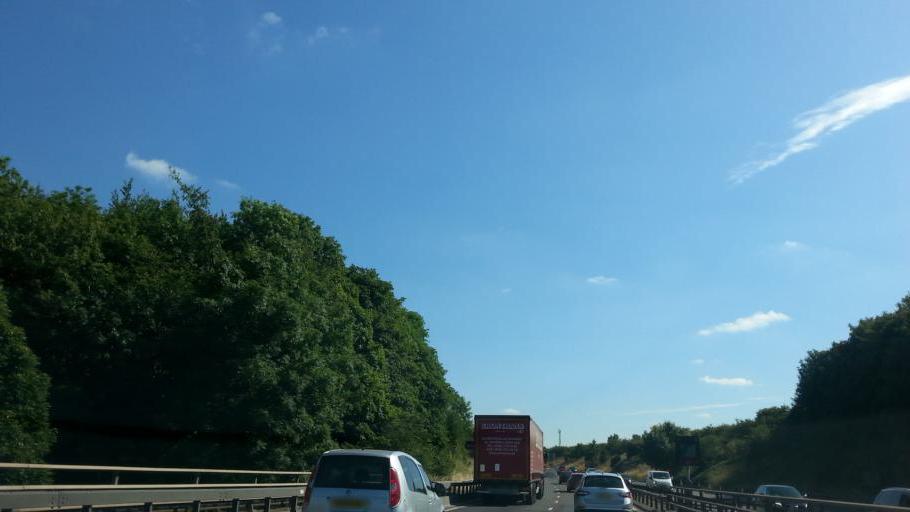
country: GB
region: England
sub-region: Doncaster
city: Bentley
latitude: 53.5077
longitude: -1.1771
